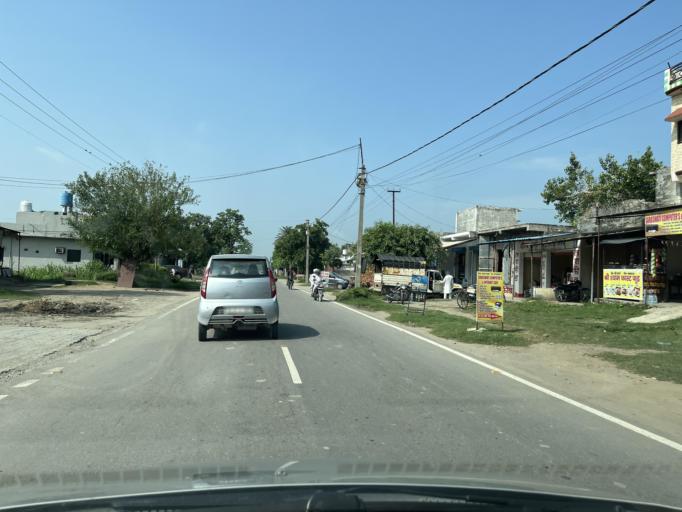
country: IN
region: Uttarakhand
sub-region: Udham Singh Nagar
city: Bazpur
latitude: 29.2077
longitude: 79.2124
